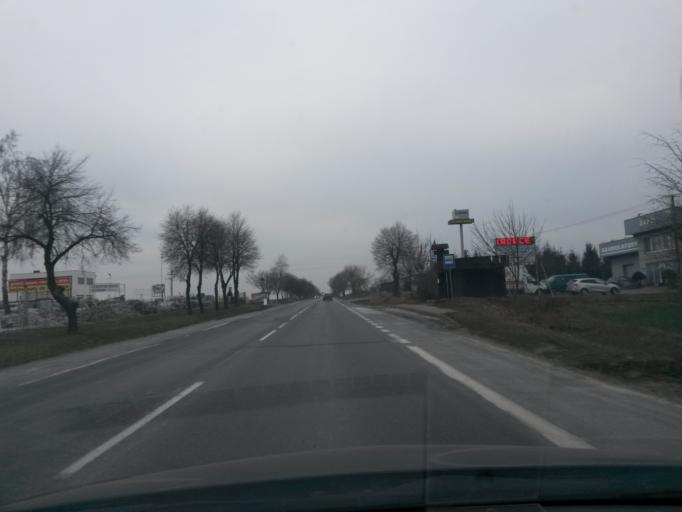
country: PL
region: Greater Poland Voivodeship
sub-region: Powiat poznanski
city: Kobylnica
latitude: 52.4663
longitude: 17.1490
